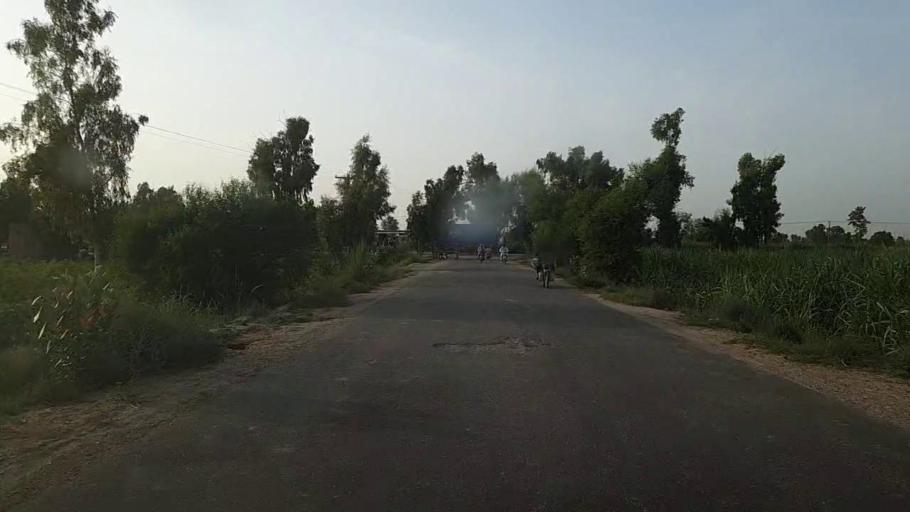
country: PK
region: Sindh
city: Ubauro
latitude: 28.1898
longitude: 69.8270
